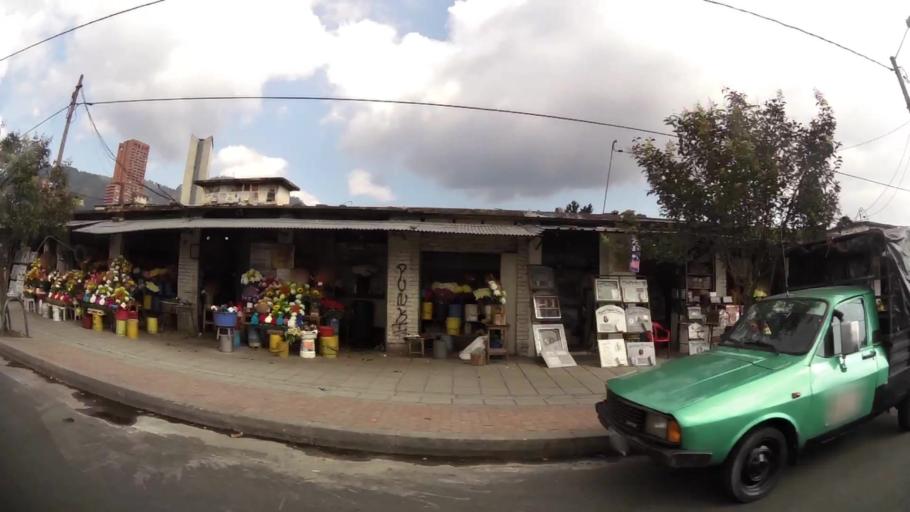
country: CO
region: Bogota D.C.
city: Bogota
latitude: 4.6176
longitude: -74.0760
